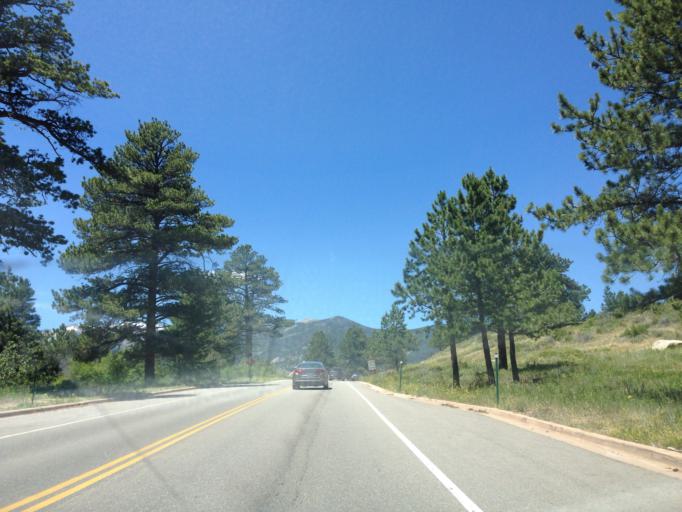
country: US
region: Colorado
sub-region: Larimer County
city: Estes Park
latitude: 40.3516
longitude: -105.5793
